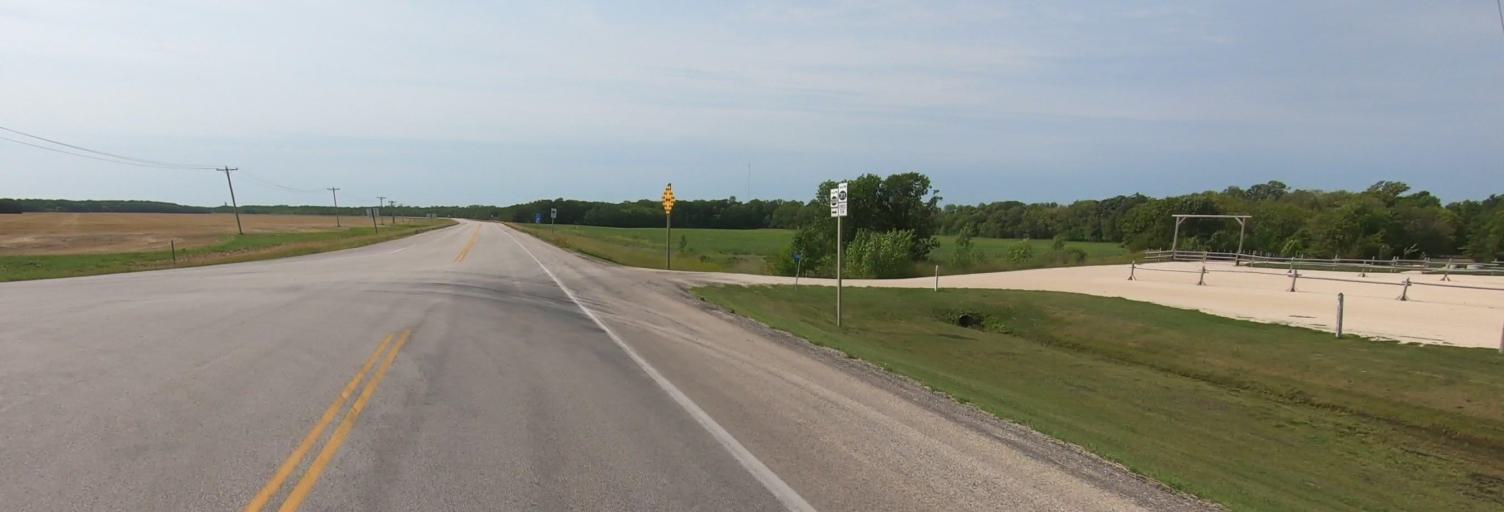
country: CA
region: Manitoba
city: Niverville
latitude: 49.6060
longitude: -97.1293
